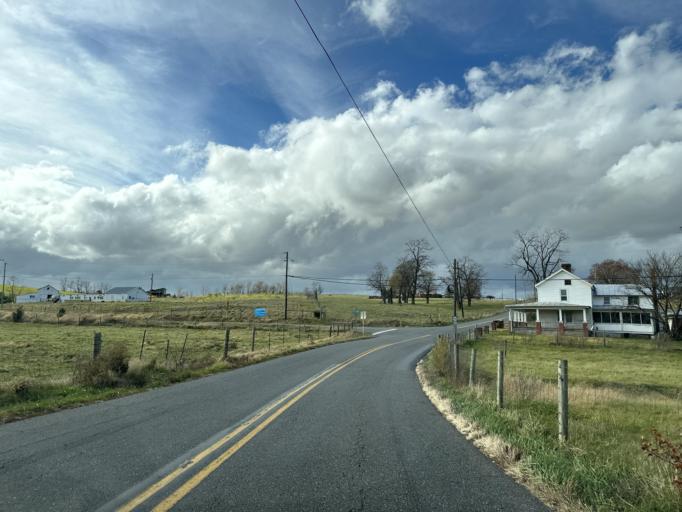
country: US
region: Virginia
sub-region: City of Harrisonburg
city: Harrisonburg
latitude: 38.4738
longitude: -78.8918
